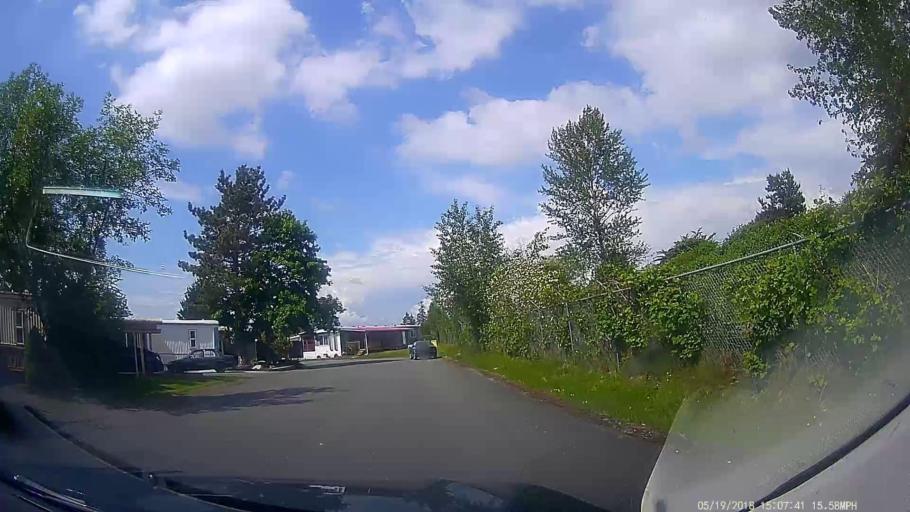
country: US
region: Washington
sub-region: Skagit County
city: Mount Vernon
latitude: 48.4175
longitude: -122.3068
